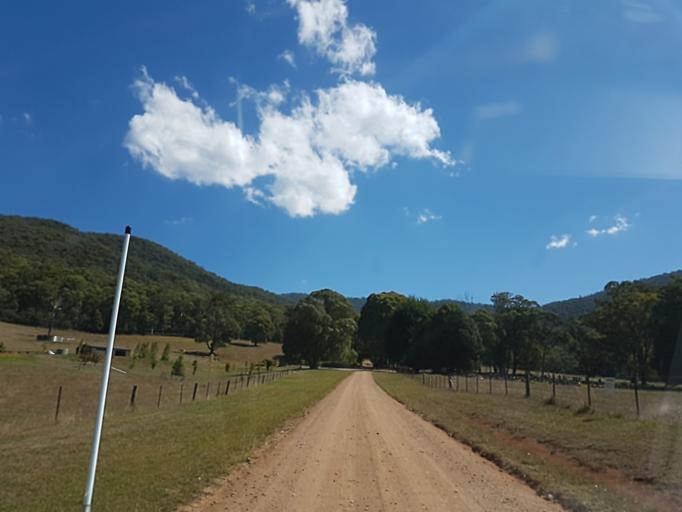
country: AU
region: Victoria
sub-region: Alpine
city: Mount Beauty
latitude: -36.8731
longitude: 147.0591
